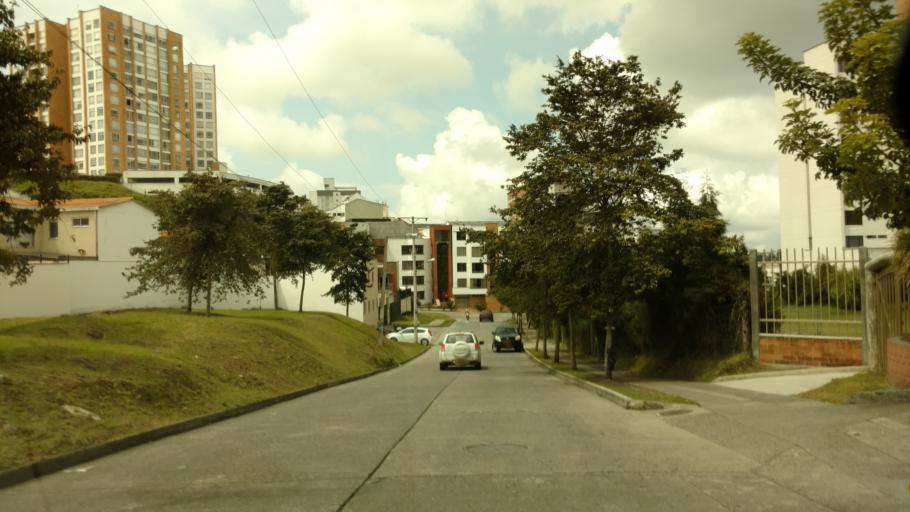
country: CO
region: Caldas
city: Villamaria
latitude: 5.0502
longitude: -75.4867
